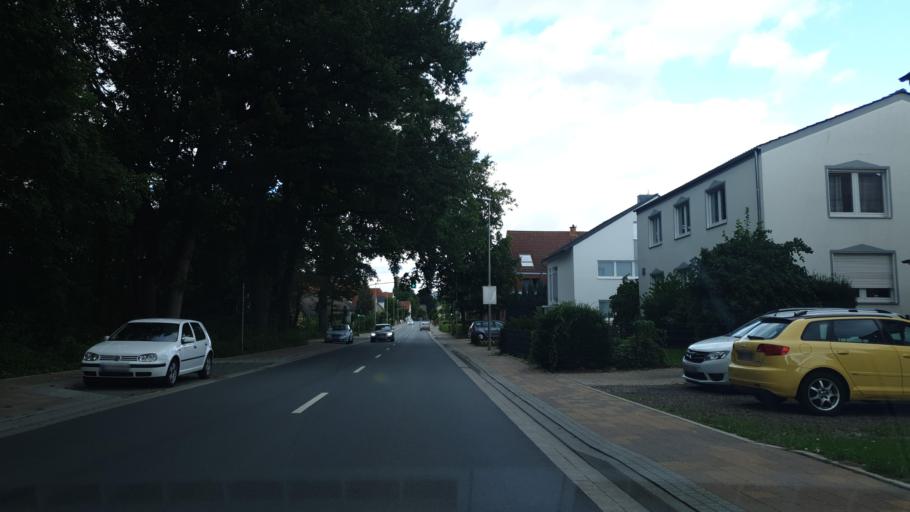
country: DE
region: North Rhine-Westphalia
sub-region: Regierungsbezirk Detmold
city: Hiddenhausen
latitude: 52.1688
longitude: 8.6152
